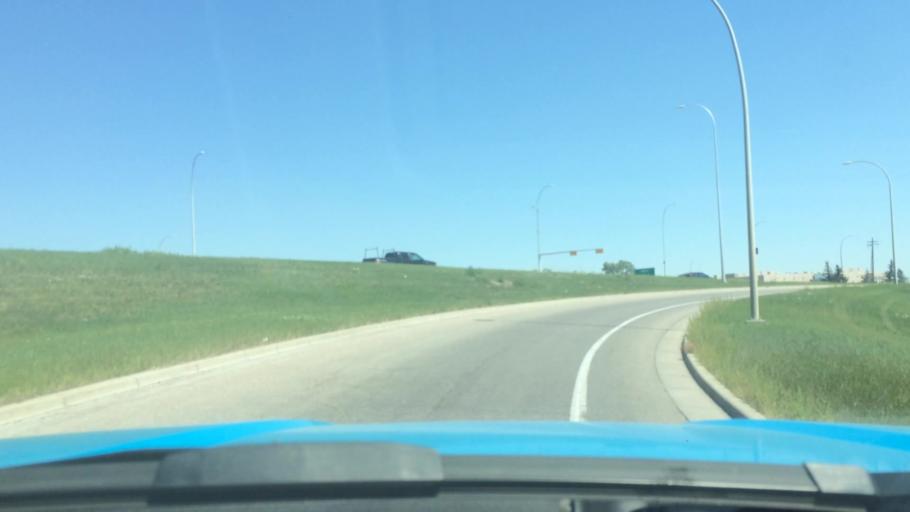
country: CA
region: Alberta
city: Calgary
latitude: 50.9499
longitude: -114.0702
